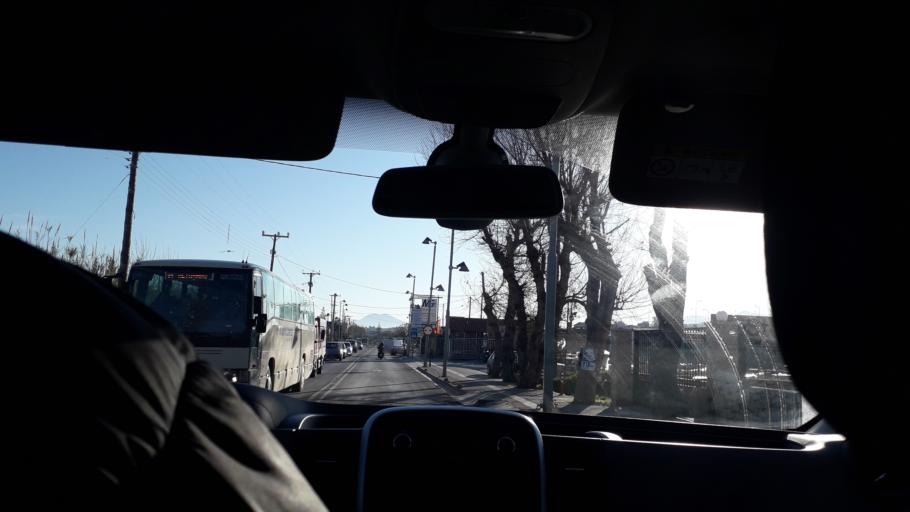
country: GR
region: Crete
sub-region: Nomos Rethymnis
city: Rethymno
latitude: 35.3660
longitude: 24.5129
